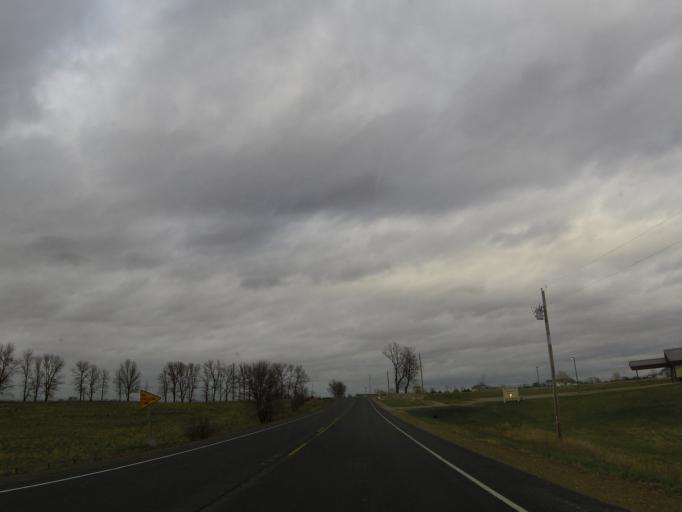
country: US
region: Wisconsin
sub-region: Saint Croix County
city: New Richmond
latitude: 45.0768
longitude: -92.5815
